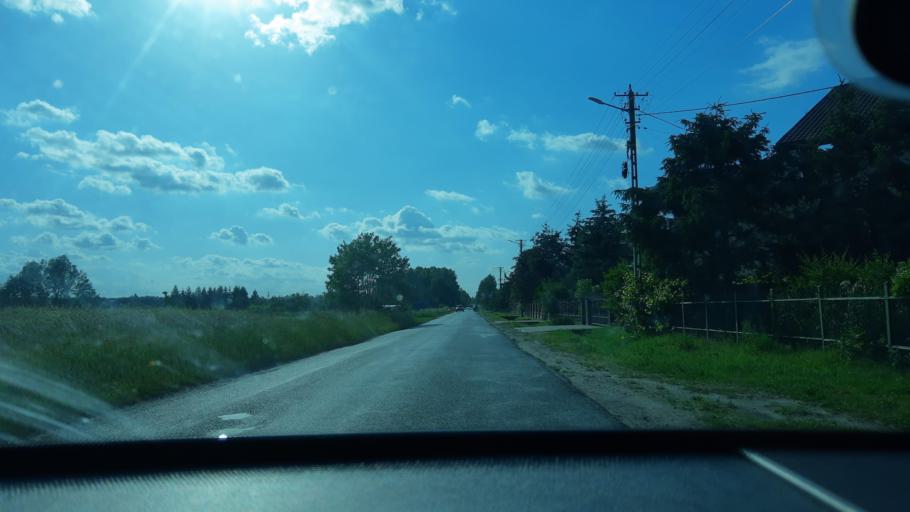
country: PL
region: Lodz Voivodeship
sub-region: Powiat zdunskowolski
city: Zapolice
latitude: 51.5404
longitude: 18.8006
